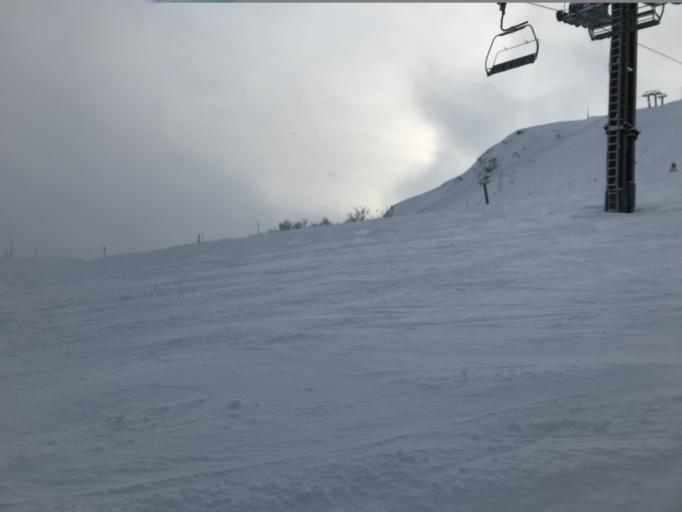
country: JP
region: Nagano
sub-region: Kitaazumi Gun
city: Hakuba
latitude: 36.6982
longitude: 137.8097
